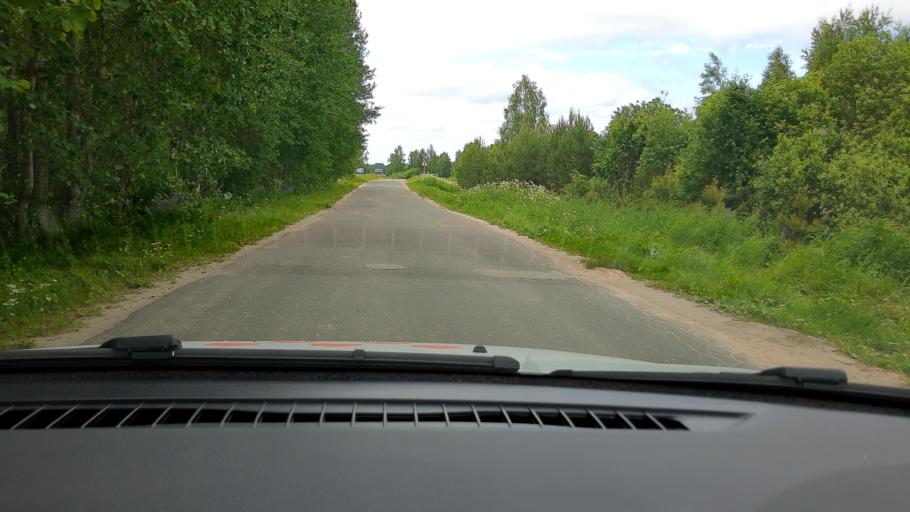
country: RU
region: Nizjnij Novgorod
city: Sitniki
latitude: 56.5242
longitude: 44.1055
